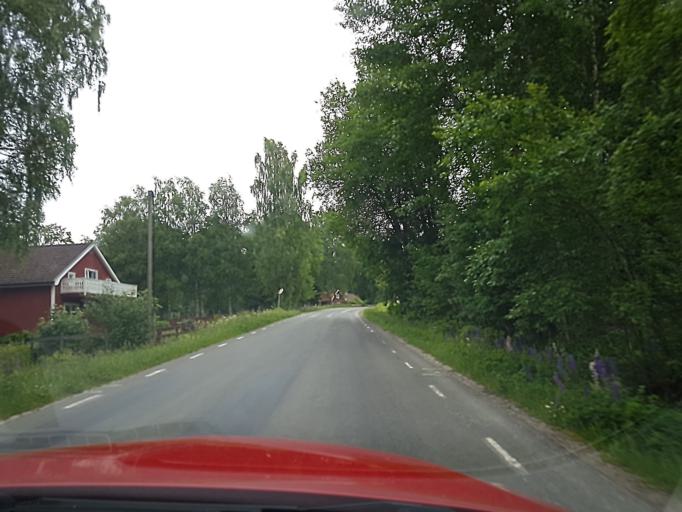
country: SE
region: Vaestra Goetaland
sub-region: Tidaholms Kommun
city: Olofstorp
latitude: 58.3298
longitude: 13.9934
